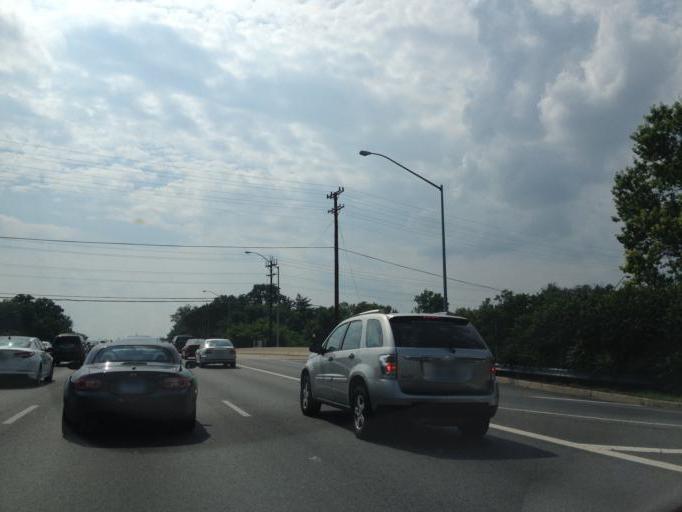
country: US
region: Maryland
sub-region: Montgomery County
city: Forest Glen
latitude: 39.0135
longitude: -77.0410
